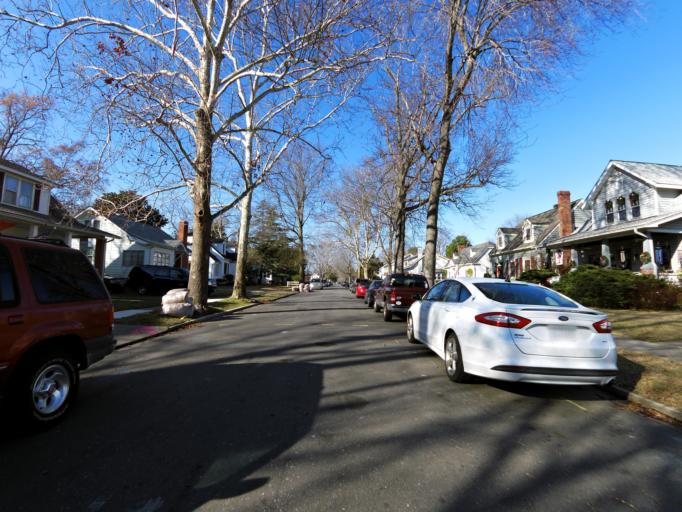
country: US
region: Virginia
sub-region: City of Hampton
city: Hampton
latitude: 37.0014
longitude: -76.3762
